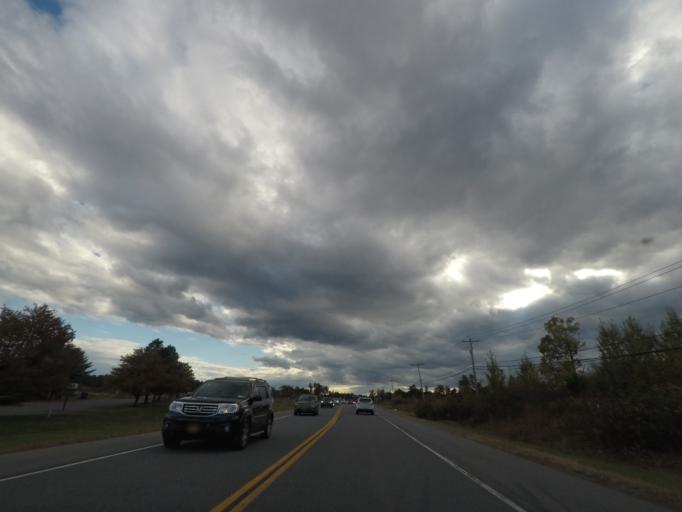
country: US
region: New York
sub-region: Albany County
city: Colonie
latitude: 42.7220
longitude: -73.8643
